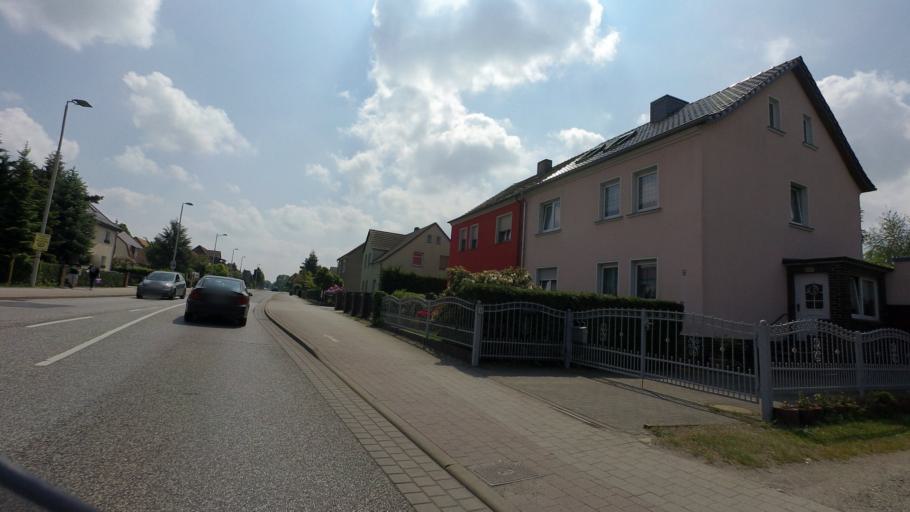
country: DE
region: Brandenburg
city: Cottbus
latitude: 51.7156
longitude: 14.3512
